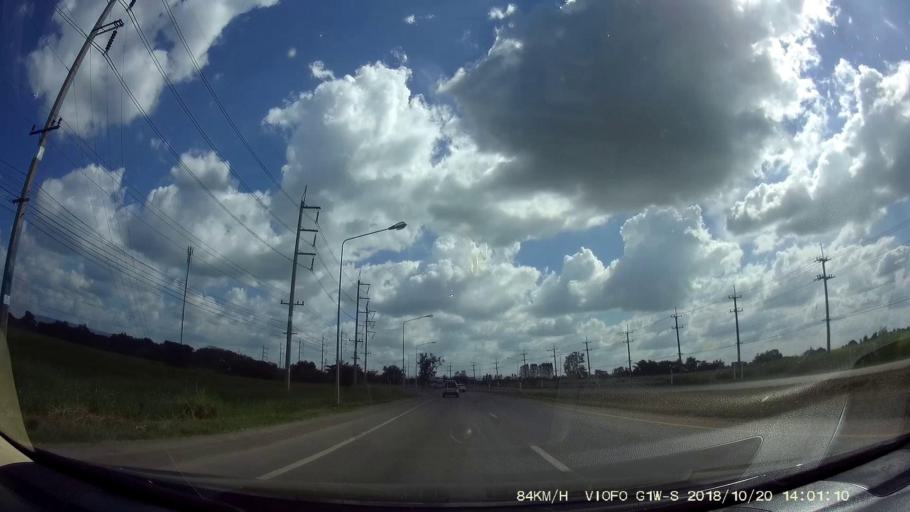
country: TH
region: Khon Kaen
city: Chum Phae
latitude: 16.5051
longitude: 102.1188
